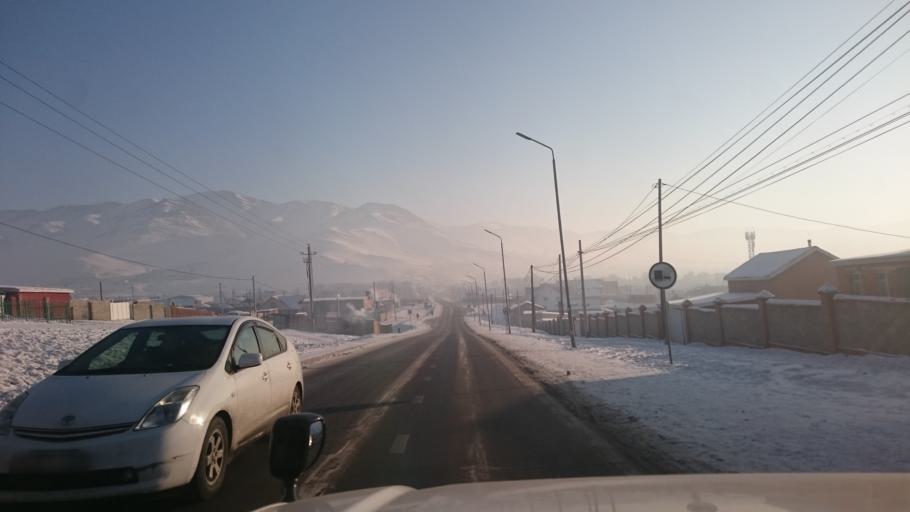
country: MN
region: Ulaanbaatar
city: Ulaanbaatar
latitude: 47.9291
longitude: 107.1515
